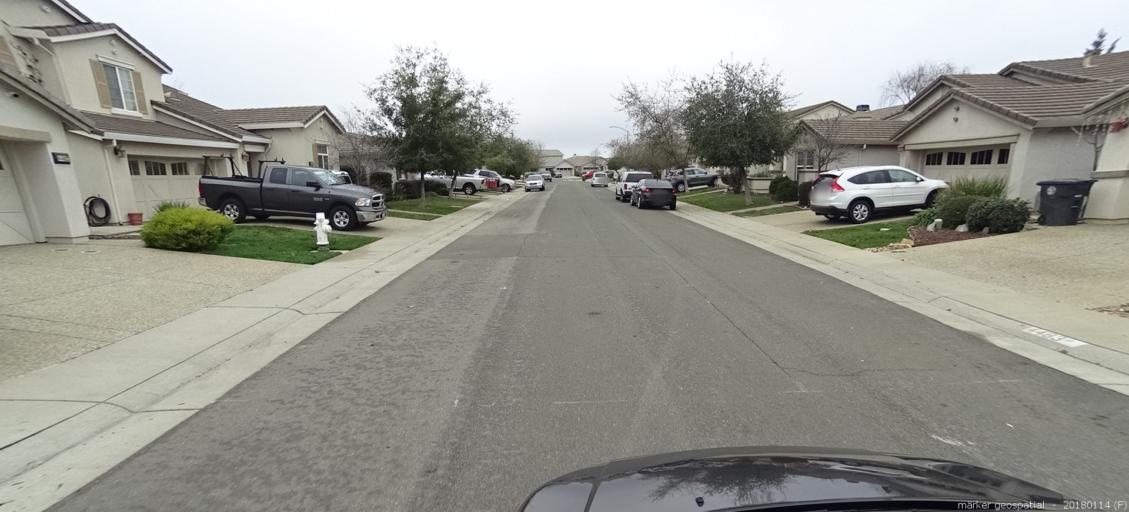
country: US
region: California
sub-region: Sacramento County
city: Rancho Cordova
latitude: 38.5401
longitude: -121.2410
